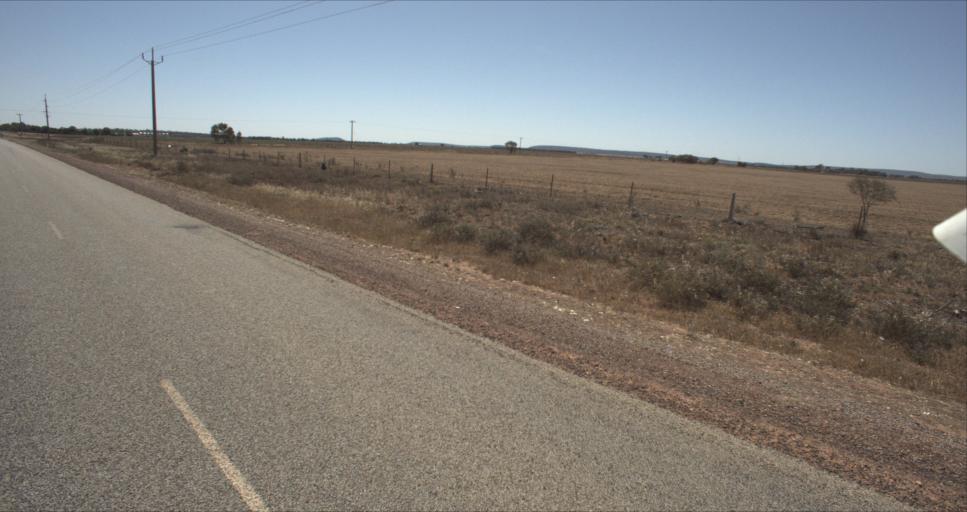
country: AU
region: New South Wales
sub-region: Leeton
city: Leeton
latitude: -34.4593
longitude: 146.2945
